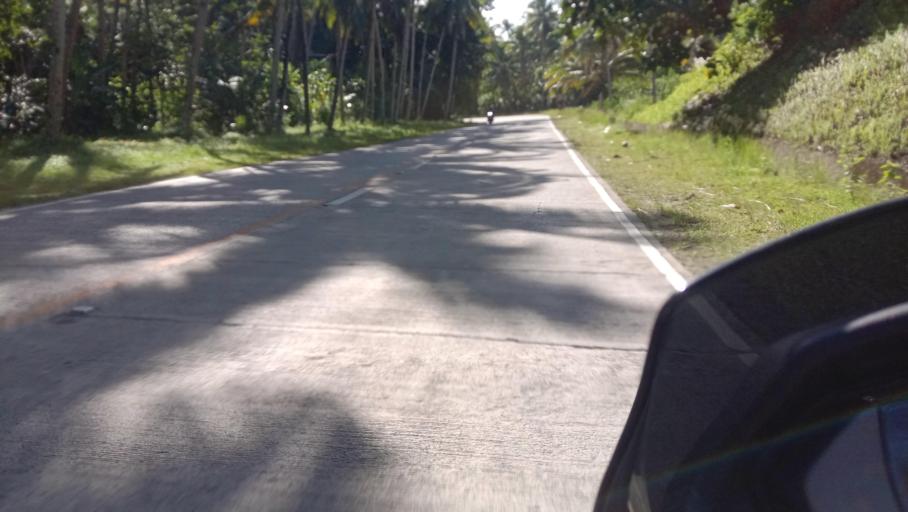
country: PH
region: Caraga
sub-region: Province of Surigao del Sur
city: Barobo
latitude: 8.5398
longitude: 126.1063
